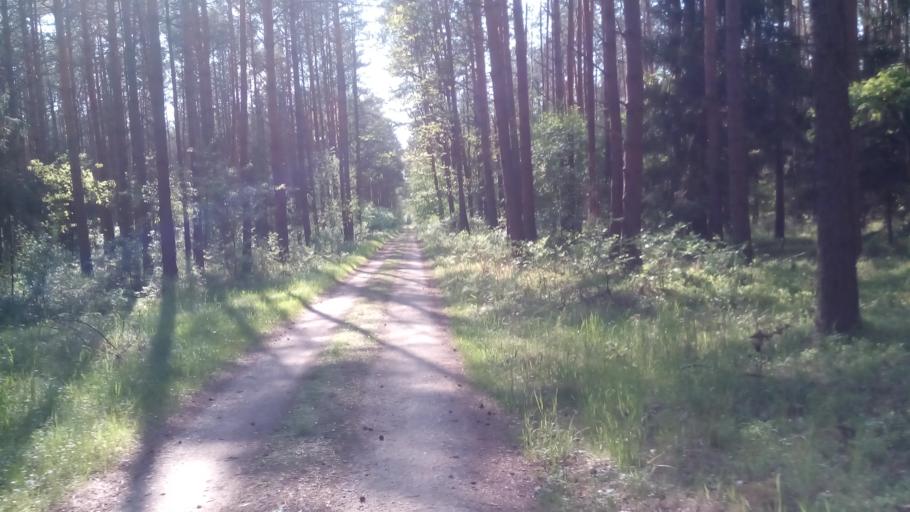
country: PL
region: Opole Voivodeship
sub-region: Powiat opolski
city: Tarnow Opolski
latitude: 50.5847
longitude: 18.0652
